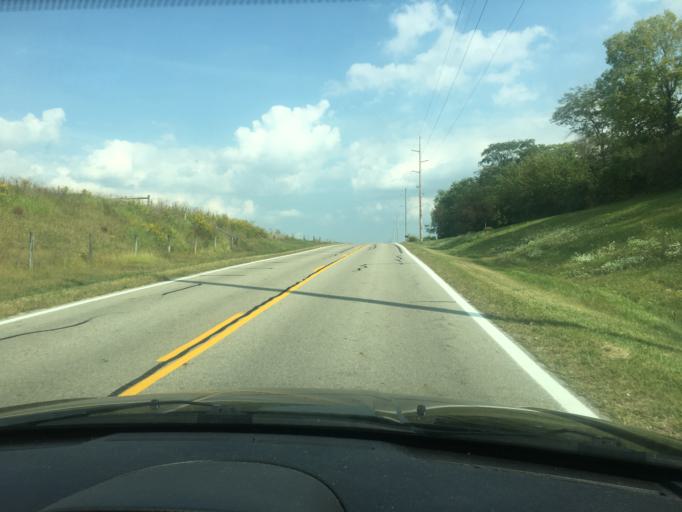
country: US
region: Ohio
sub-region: Champaign County
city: Urbana
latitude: 40.1282
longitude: -83.7843
